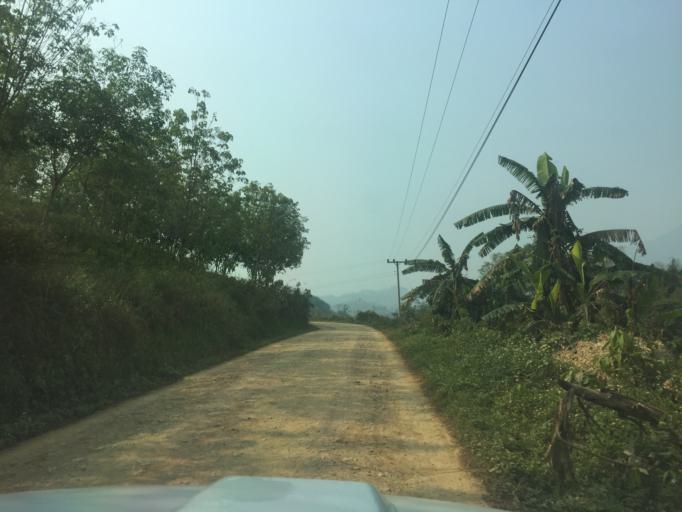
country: TH
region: Phayao
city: Phu Sang
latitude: 19.6537
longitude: 100.5272
